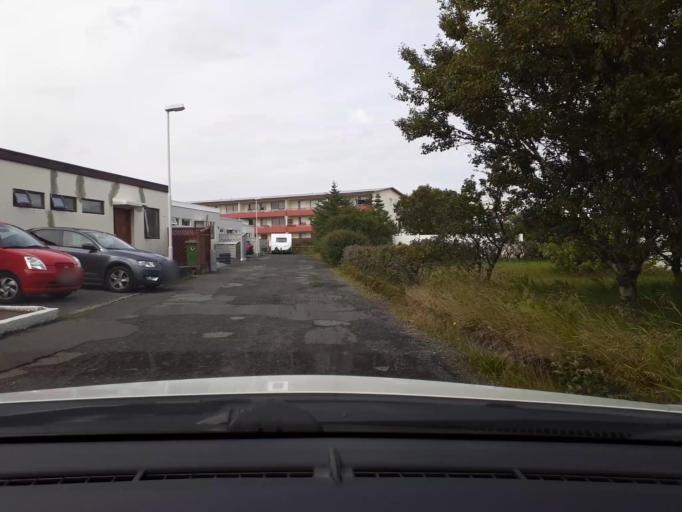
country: IS
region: Southern Peninsula
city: Reykjanesbaer
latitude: 63.9885
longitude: -22.5541
